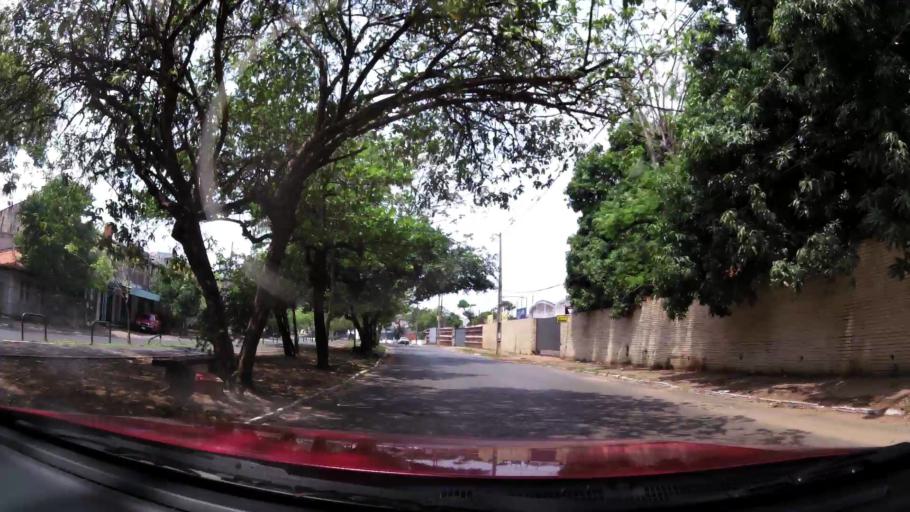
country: PY
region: Central
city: Fernando de la Mora
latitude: -25.3171
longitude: -57.5661
